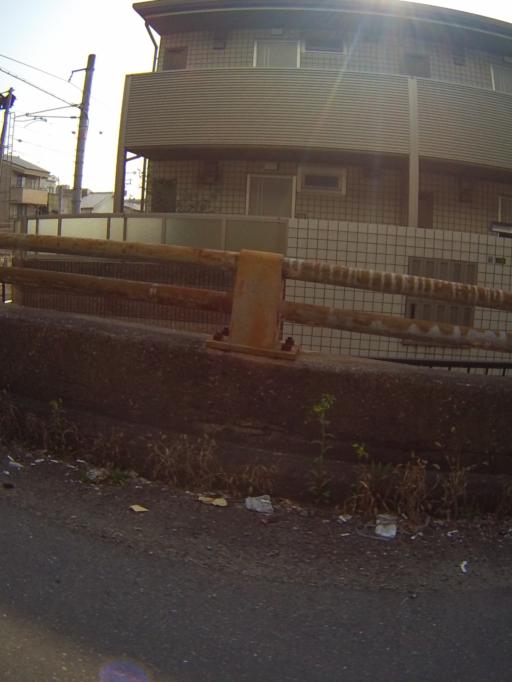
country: JP
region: Osaka
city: Osaka-shi
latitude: 34.6801
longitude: 135.4555
